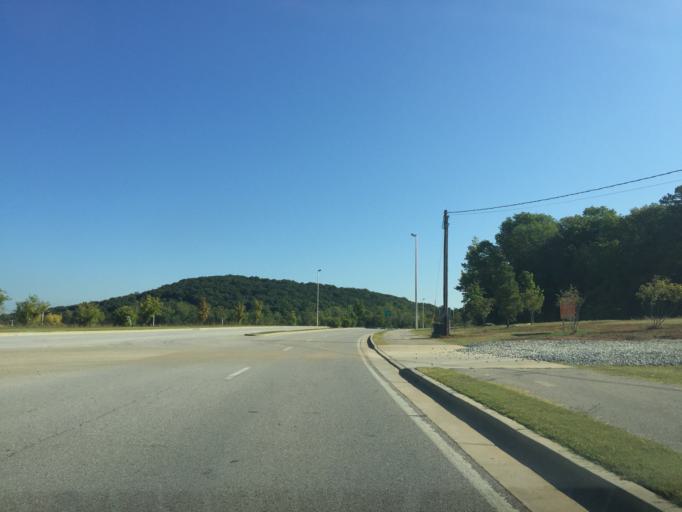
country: US
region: Tennessee
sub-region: Hamilton County
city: Harrison
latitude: 35.0748
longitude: -85.1306
